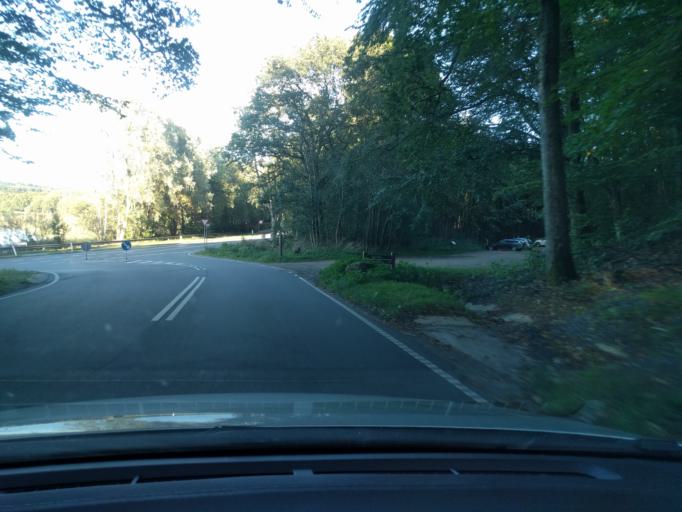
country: DK
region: Central Jutland
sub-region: Skanderborg Kommune
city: Ry
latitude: 56.0970
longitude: 9.7809
